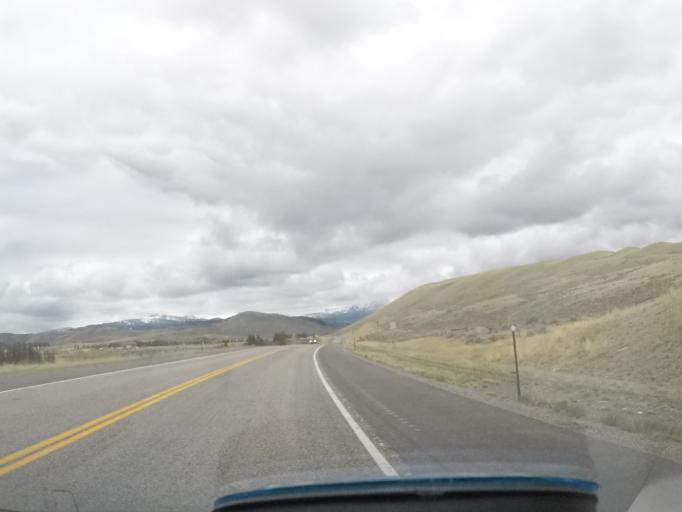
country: US
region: Wyoming
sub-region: Sublette County
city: Pinedale
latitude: 43.5877
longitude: -109.7717
